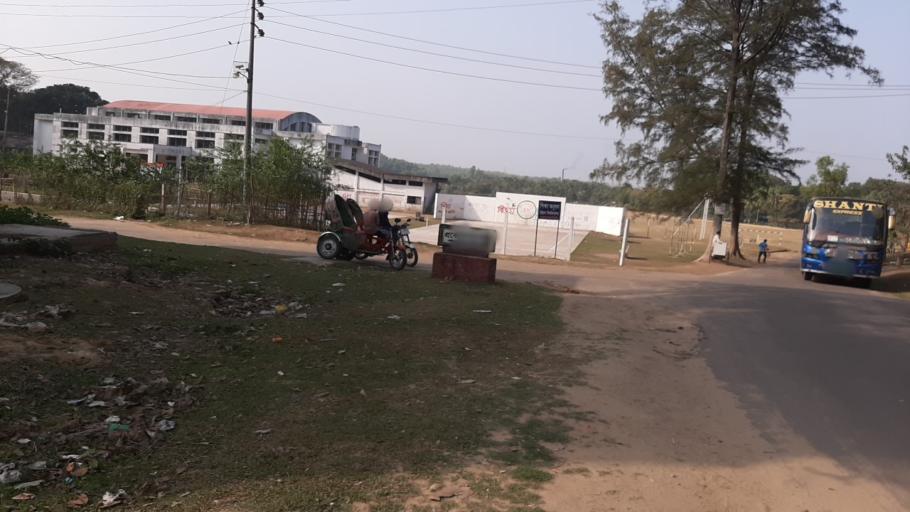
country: BD
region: Chittagong
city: Raojan
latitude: 22.4786
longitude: 91.7908
